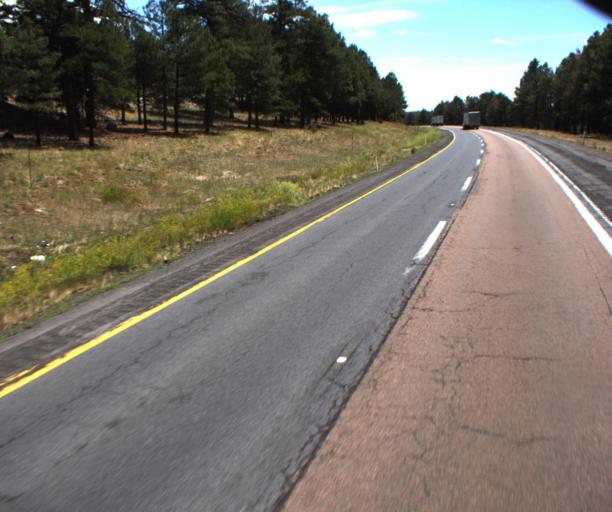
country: US
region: Arizona
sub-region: Coconino County
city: Flagstaff
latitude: 35.2047
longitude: -111.7687
